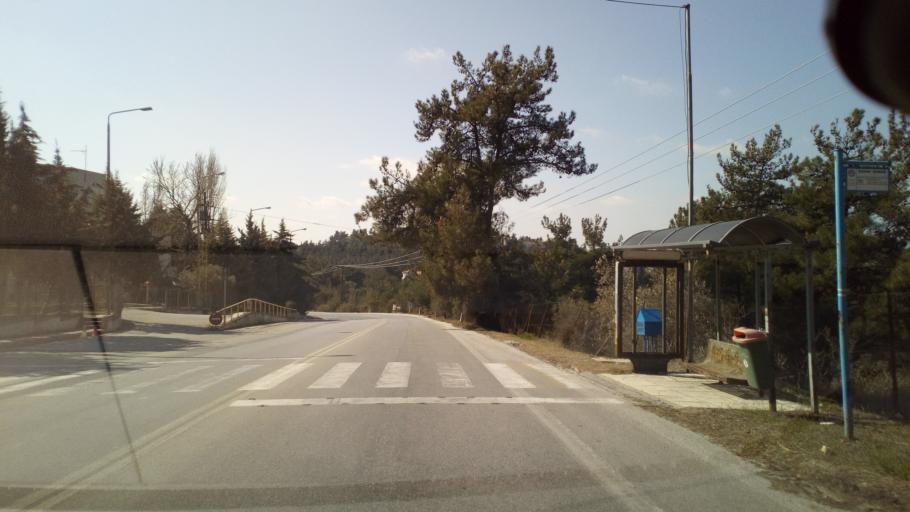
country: GR
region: Central Macedonia
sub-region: Nomos Thessalonikis
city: Panorama
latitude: 40.5978
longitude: 23.0486
